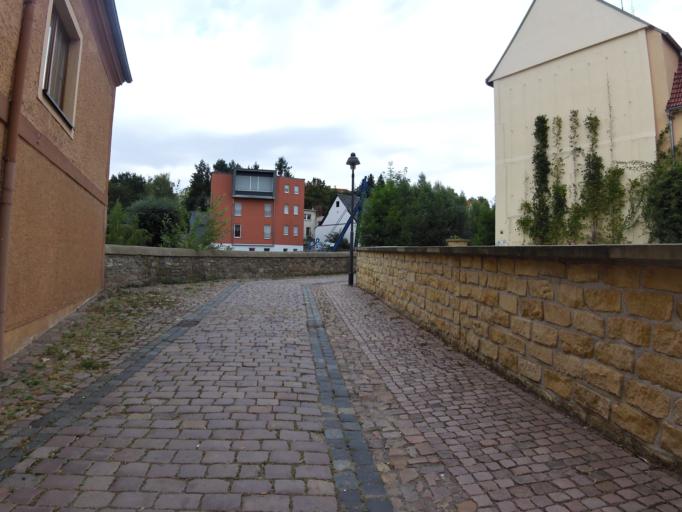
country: DE
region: Saxony
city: Dobeln
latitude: 51.1225
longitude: 13.1210
